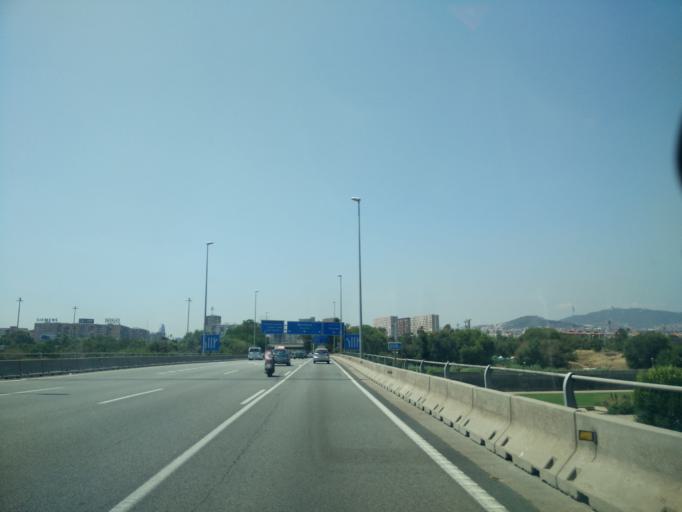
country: ES
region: Catalonia
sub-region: Provincia de Barcelona
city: Sant Adria de Besos
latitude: 41.4277
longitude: 2.2187
